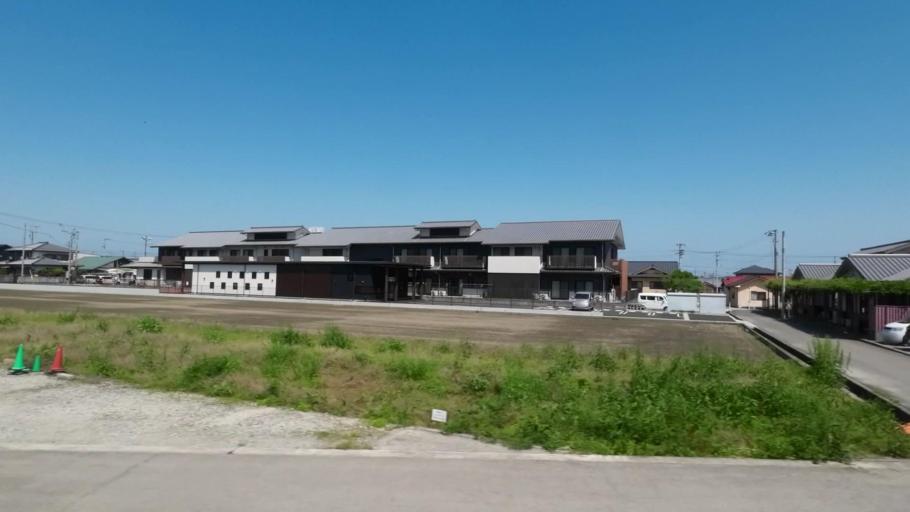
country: JP
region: Ehime
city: Niihama
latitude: 33.9614
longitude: 133.3105
